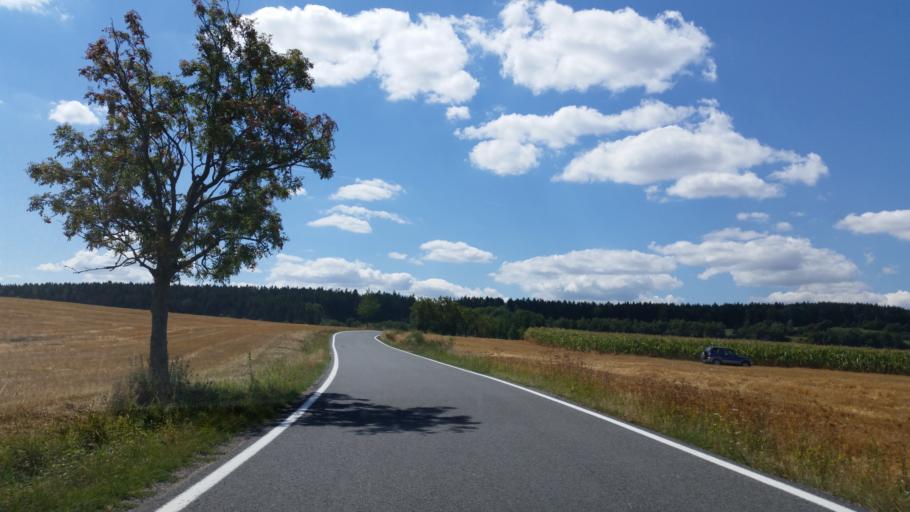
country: CZ
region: Vysocina
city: Lipa
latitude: 49.4974
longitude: 15.5281
